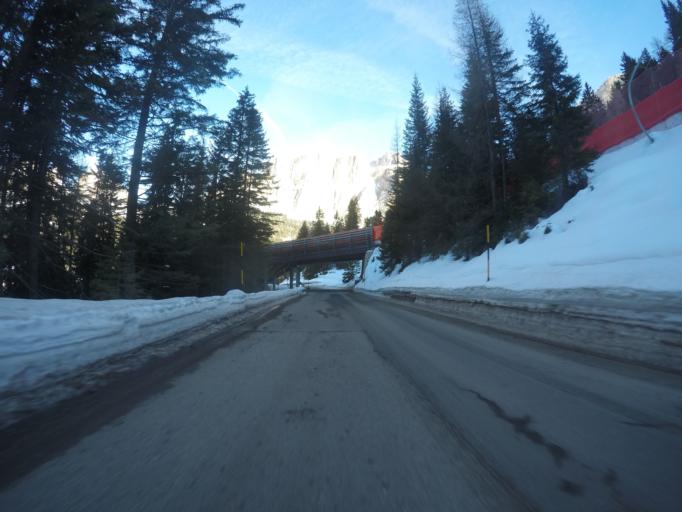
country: IT
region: Trentino-Alto Adige
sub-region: Provincia di Trento
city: Canazei
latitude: 46.4905
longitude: 11.7875
